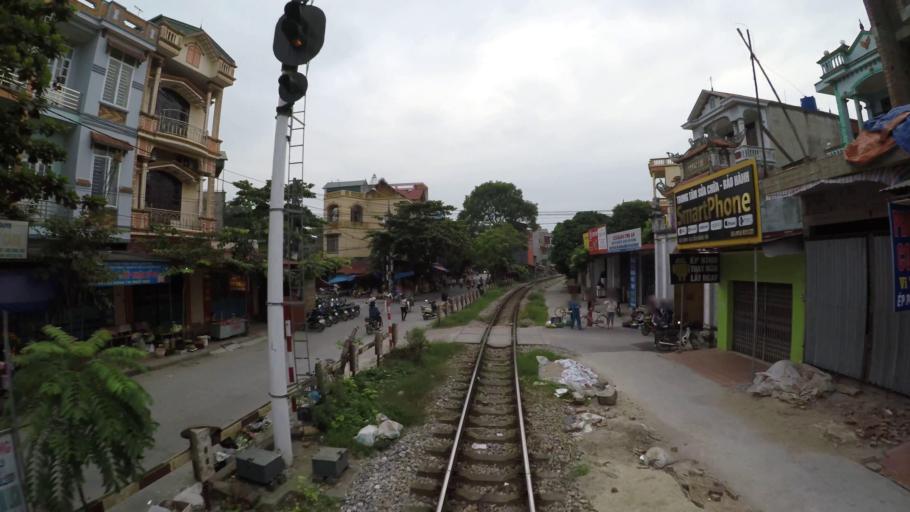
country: VN
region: Hai Duong
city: Ke Sat
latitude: 20.9663
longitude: 106.1433
